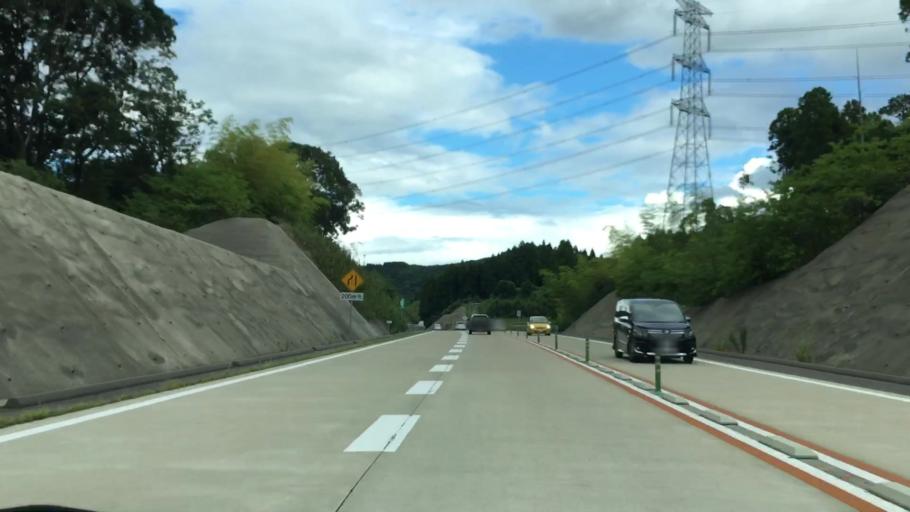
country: JP
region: Saga Prefecture
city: Imaricho-ko
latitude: 33.3554
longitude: 129.9267
